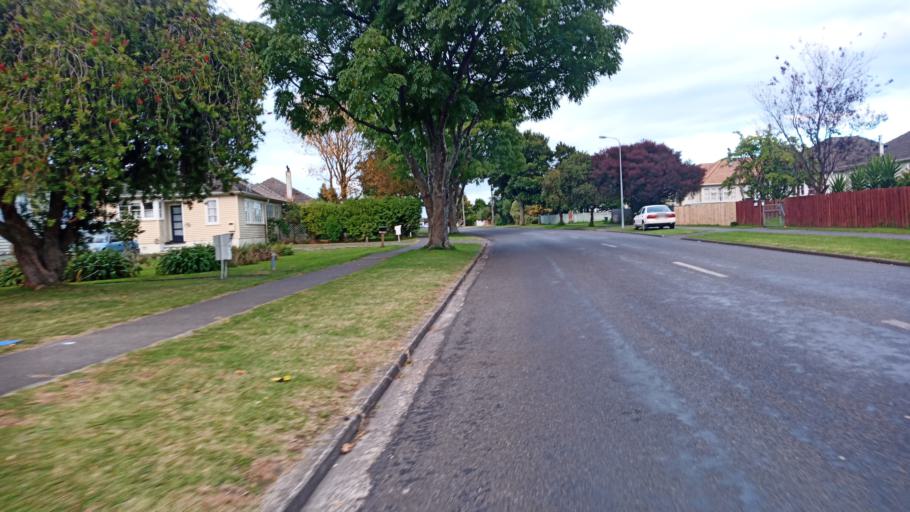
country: NZ
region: Gisborne
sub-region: Gisborne District
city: Gisborne
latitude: -38.6560
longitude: 178.0039
